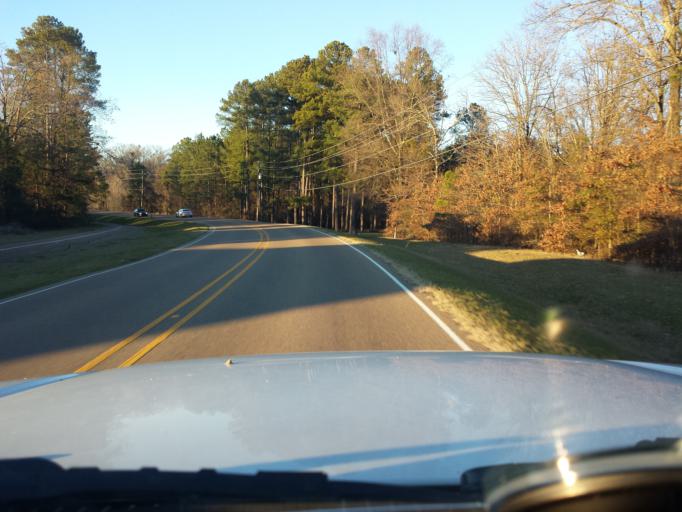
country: US
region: Mississippi
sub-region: Madison County
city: Madison
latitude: 32.4116
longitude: -90.0088
